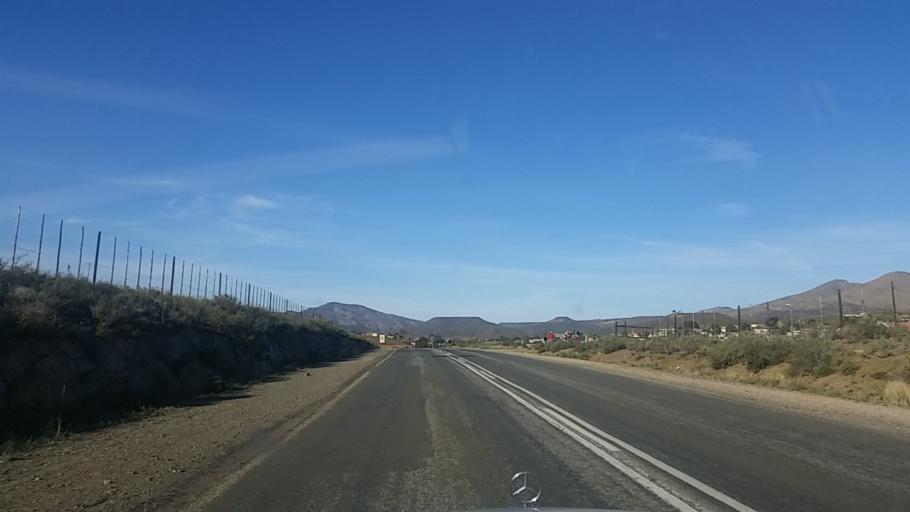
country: ZA
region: Western Cape
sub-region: Eden District Municipality
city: Knysna
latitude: -33.6655
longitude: 23.1041
